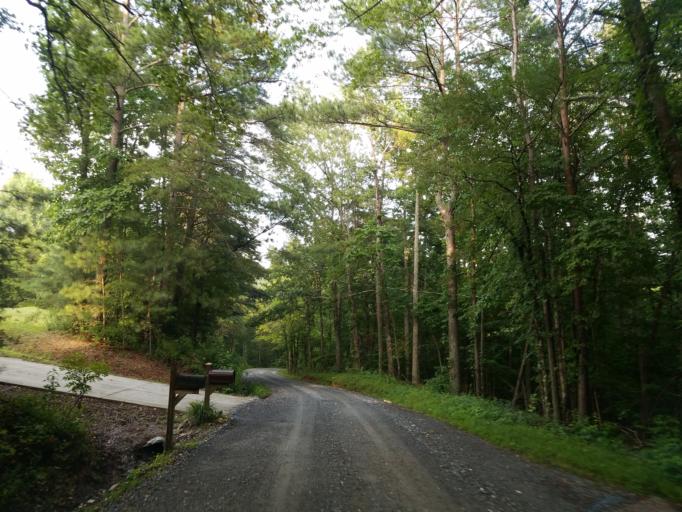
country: US
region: Georgia
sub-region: Pickens County
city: Jasper
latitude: 34.5468
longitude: -84.4453
